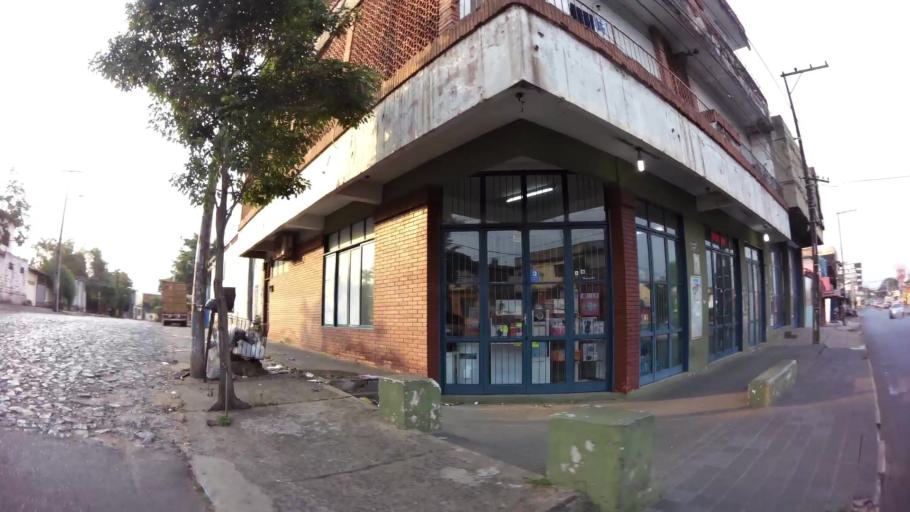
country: PY
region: Central
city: Lambare
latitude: -25.3179
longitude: -57.5756
